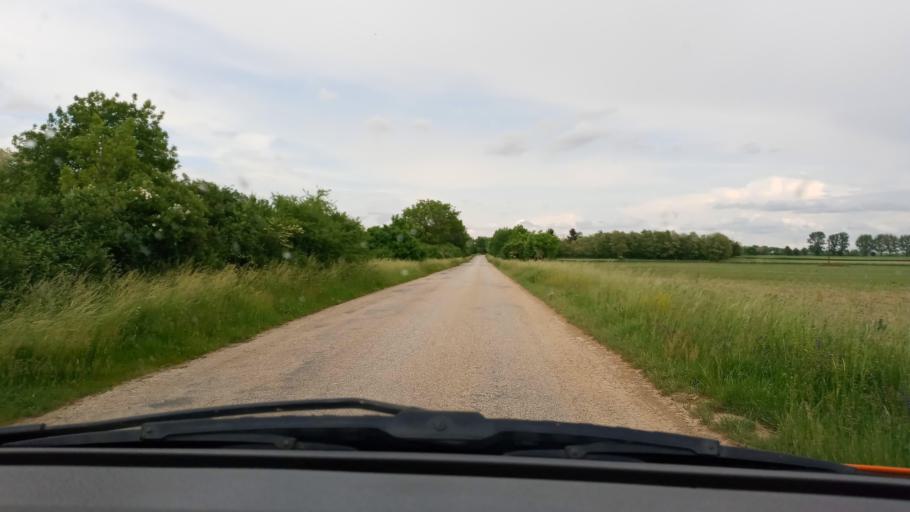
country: HU
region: Baranya
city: Harkany
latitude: 45.9164
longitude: 18.1536
